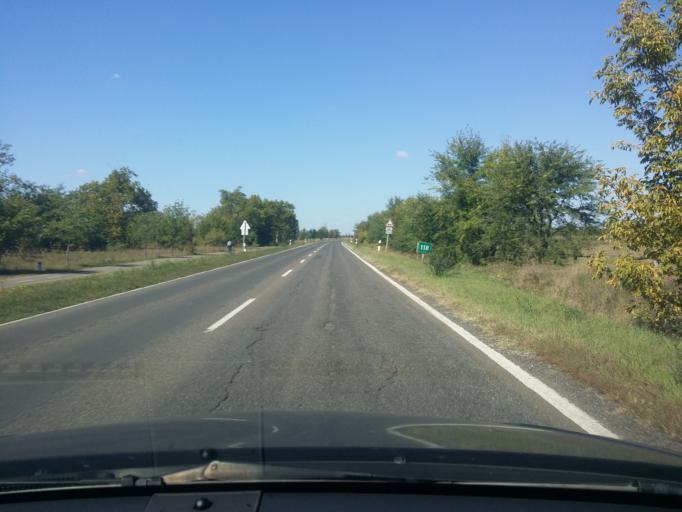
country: HU
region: Bacs-Kiskun
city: Kiskunfelegyhaza
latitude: 46.6639
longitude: 19.8636
